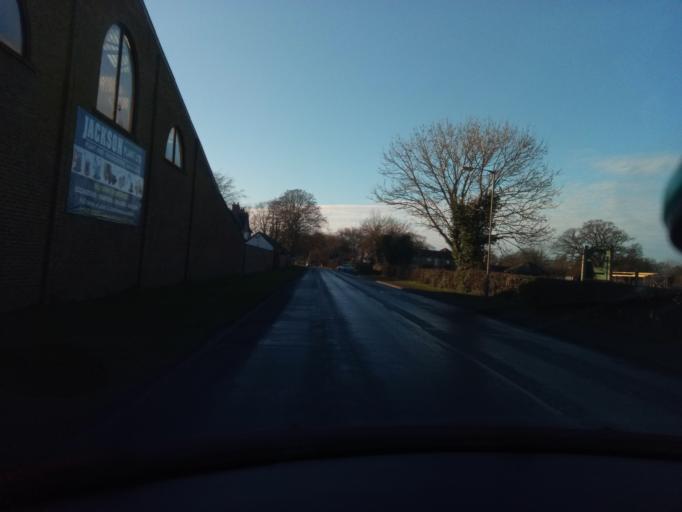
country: GB
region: England
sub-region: North Yorkshire
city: Thirsk
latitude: 54.2272
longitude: -1.3835
